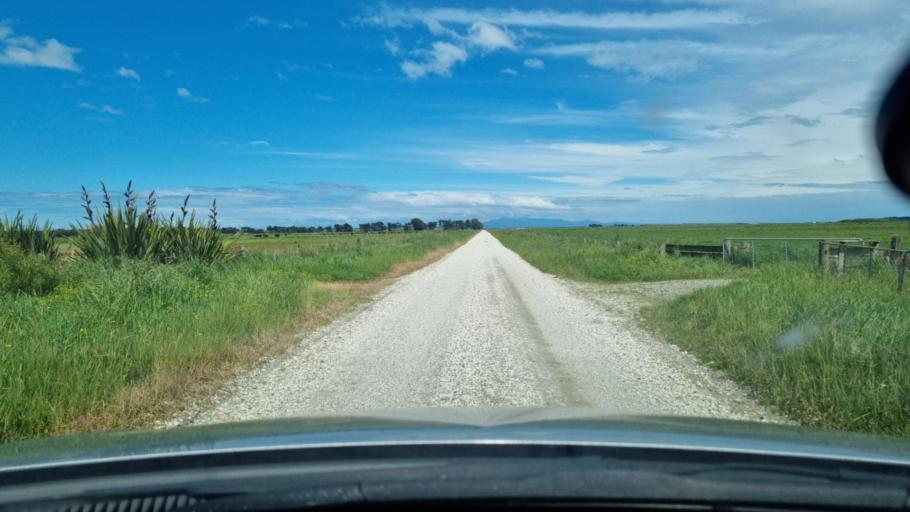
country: NZ
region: Southland
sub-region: Invercargill City
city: Invercargill
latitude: -46.3752
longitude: 168.2747
